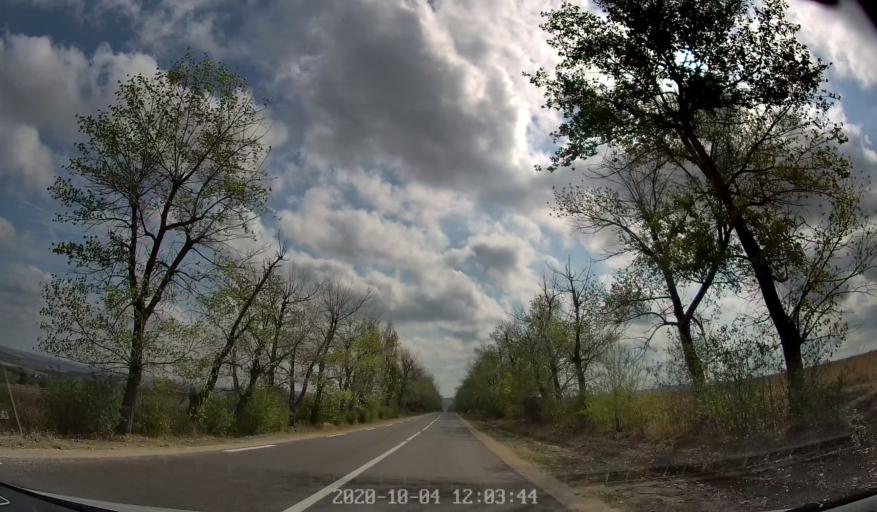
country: MD
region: Rezina
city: Saharna
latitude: 47.6098
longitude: 28.9325
